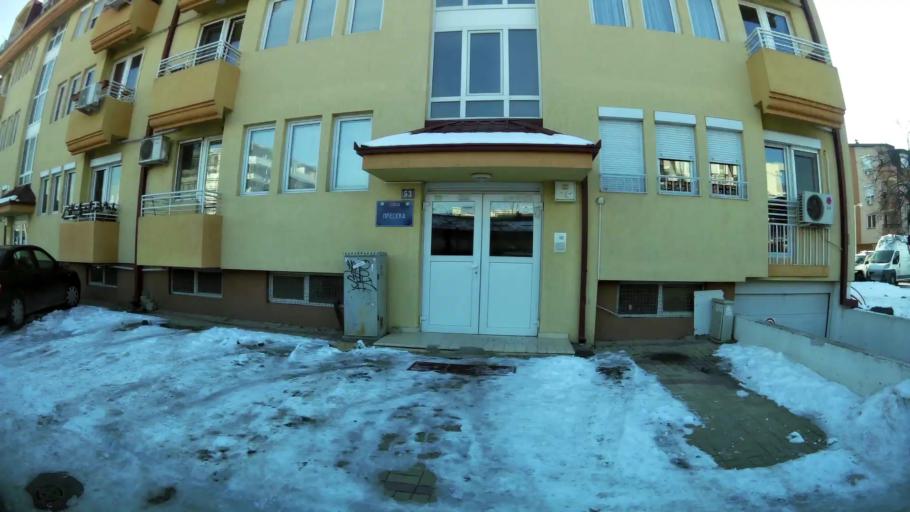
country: MK
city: Krushopek
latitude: 42.0034
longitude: 21.3766
